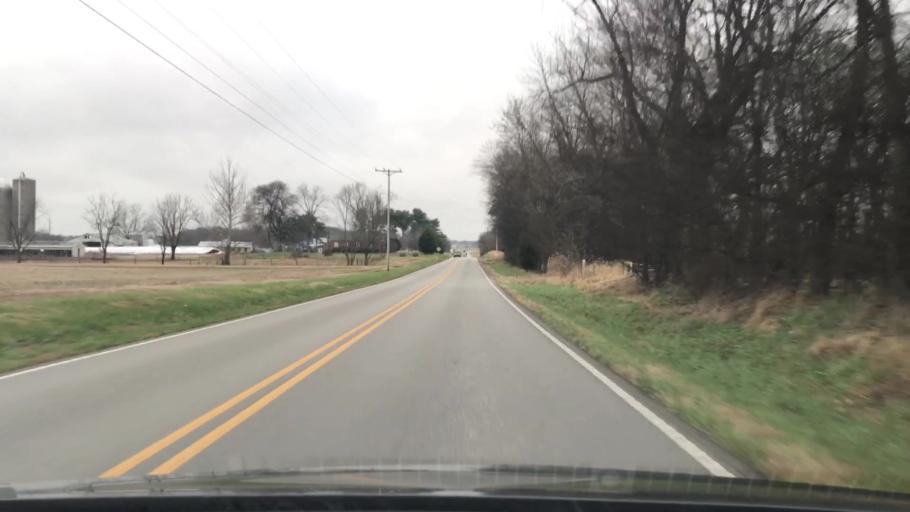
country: US
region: Kentucky
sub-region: Todd County
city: Guthrie
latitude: 36.6933
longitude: -87.2008
